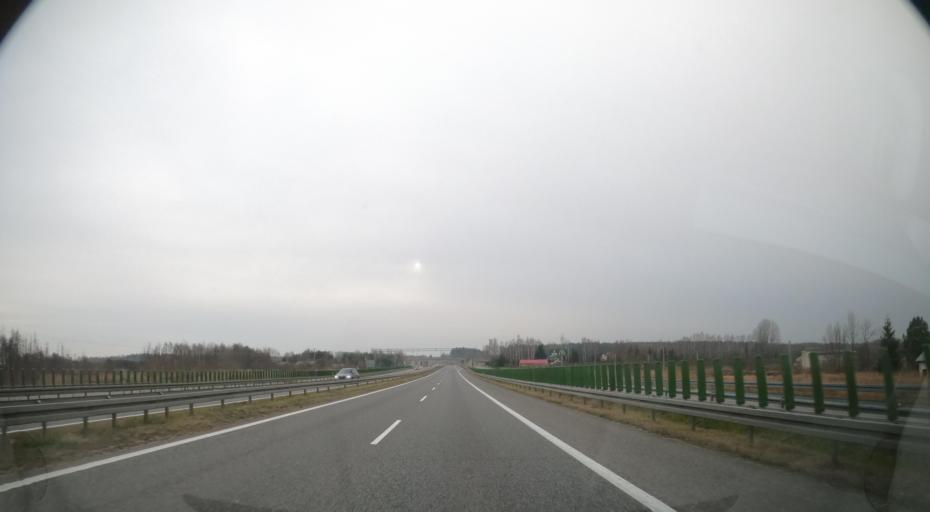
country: PL
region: Masovian Voivodeship
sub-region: Powiat grojecki
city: Grojec
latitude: 51.9030
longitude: 20.8588
